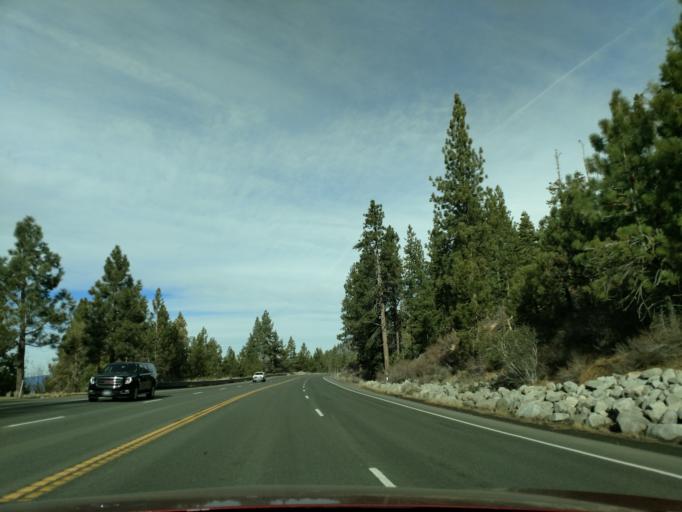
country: US
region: Nevada
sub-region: Douglas County
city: Kingsbury
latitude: 39.0520
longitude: -119.9441
